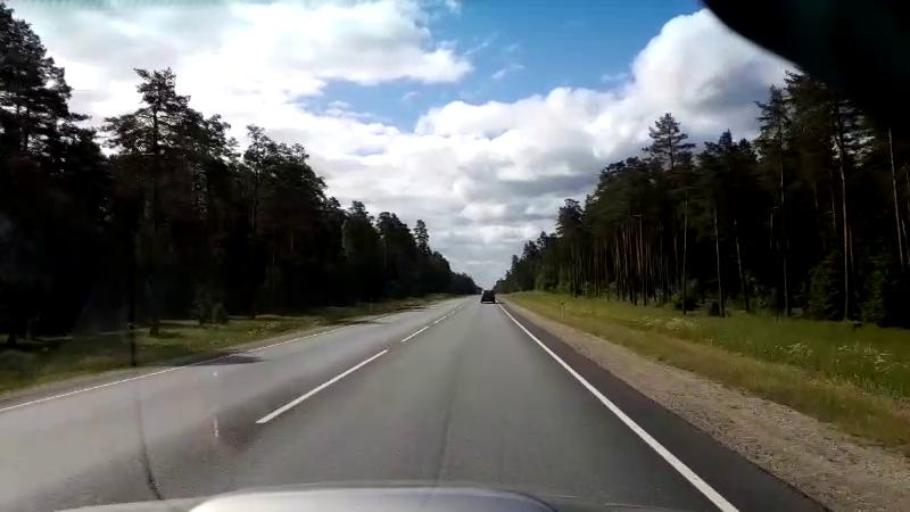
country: EE
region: Raplamaa
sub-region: Maerjamaa vald
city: Marjamaa
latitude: 59.0157
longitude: 24.4534
